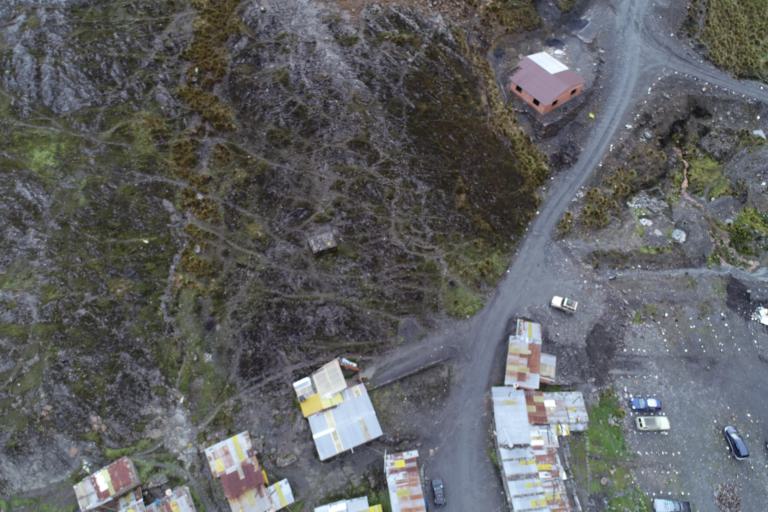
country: BO
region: La Paz
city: Sorata
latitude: -15.6627
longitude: -68.5119
